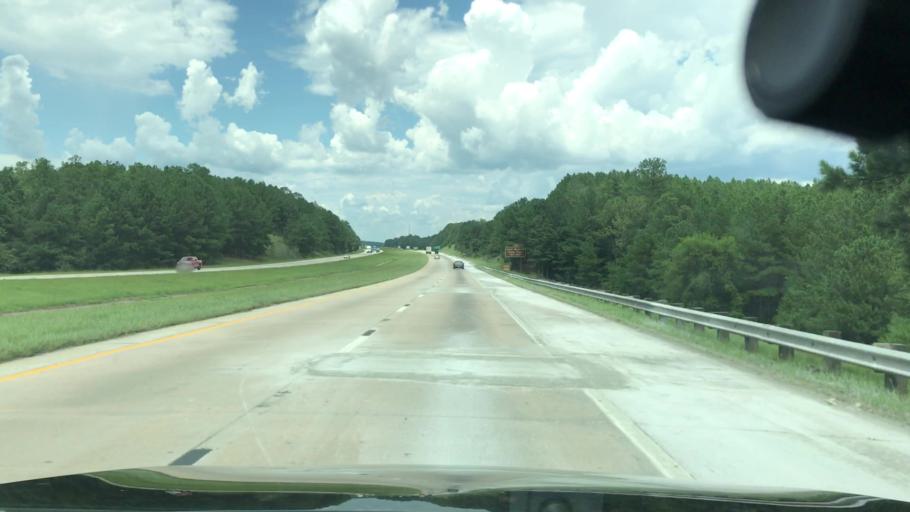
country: US
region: South Carolina
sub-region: Fairfield County
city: Winnsboro
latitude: 34.3937
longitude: -80.9937
